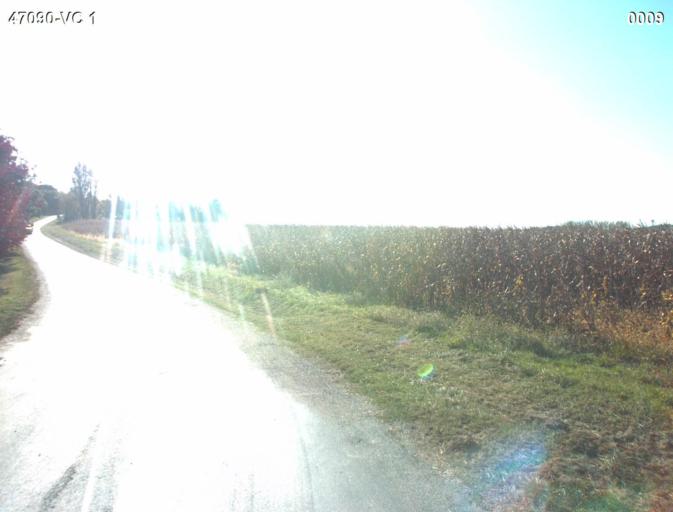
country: FR
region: Aquitaine
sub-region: Departement du Lot-et-Garonne
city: Nerac
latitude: 44.1707
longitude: 0.3729
